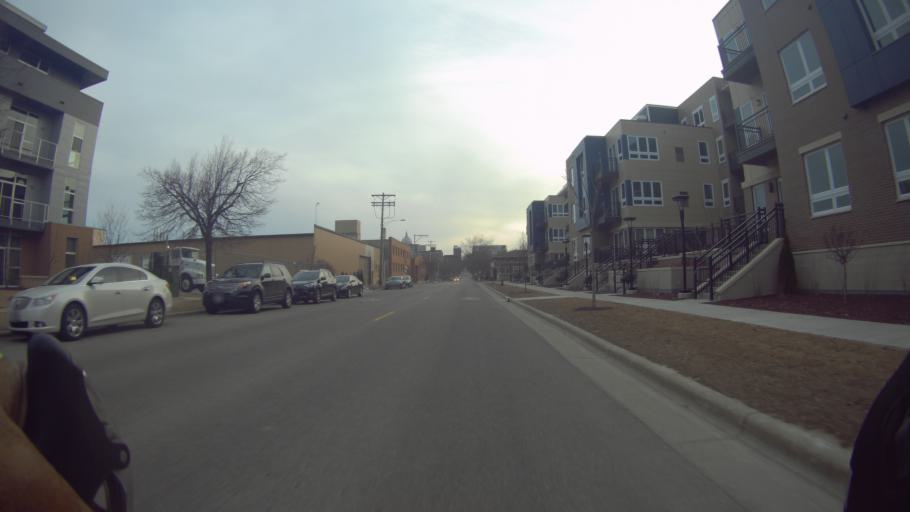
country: US
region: Wisconsin
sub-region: Dane County
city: Madison
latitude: 43.0817
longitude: -89.3765
